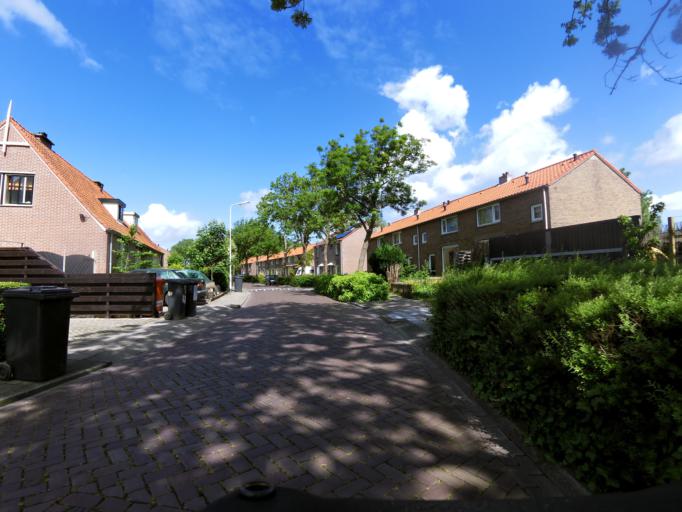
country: NL
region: Zeeland
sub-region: Schouwen-Duiveland
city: Bruinisse
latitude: 51.6900
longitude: 3.9851
